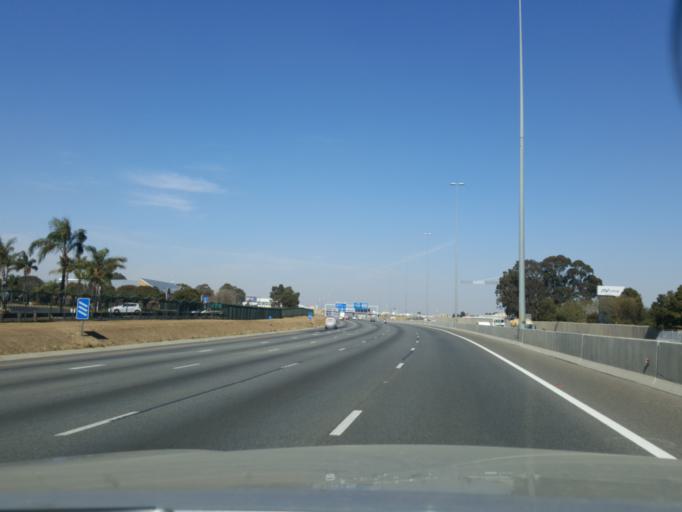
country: ZA
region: Gauteng
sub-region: Ekurhuleni Metropolitan Municipality
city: Boksburg
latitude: -26.1472
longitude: 28.2200
